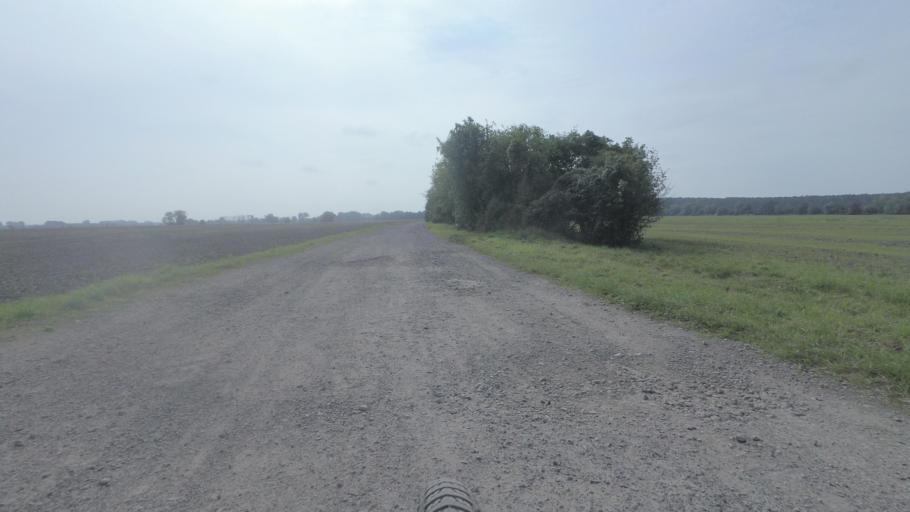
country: DE
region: Brandenburg
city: Rangsdorf
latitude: 52.2777
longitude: 13.3872
